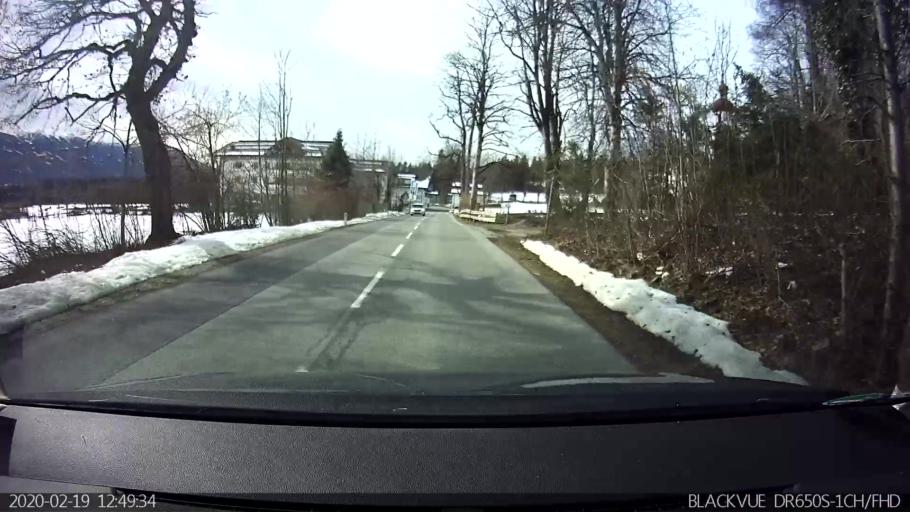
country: AT
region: Tyrol
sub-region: Politischer Bezirk Innsbruck Land
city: Gnadenwald
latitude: 47.3204
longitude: 11.5553
